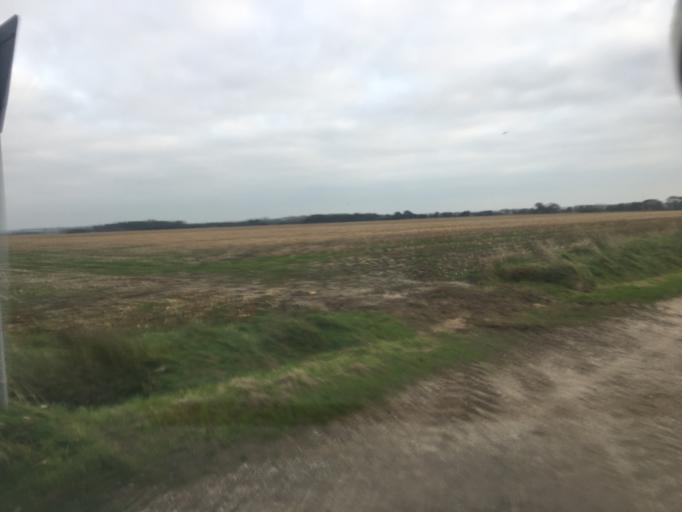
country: DE
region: Schleswig-Holstein
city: Rodenas
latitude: 54.9627
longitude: 8.7390
